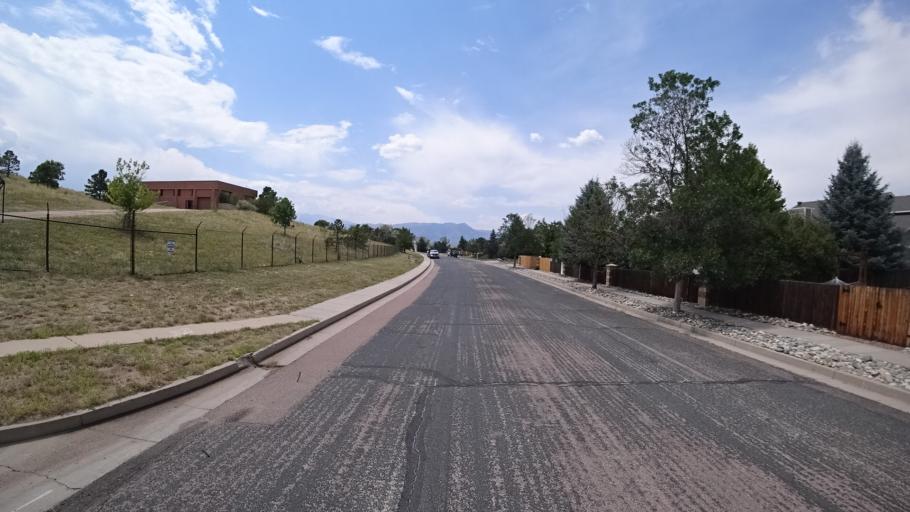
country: US
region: Colorado
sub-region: El Paso County
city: Black Forest
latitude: 38.9594
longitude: -104.7683
